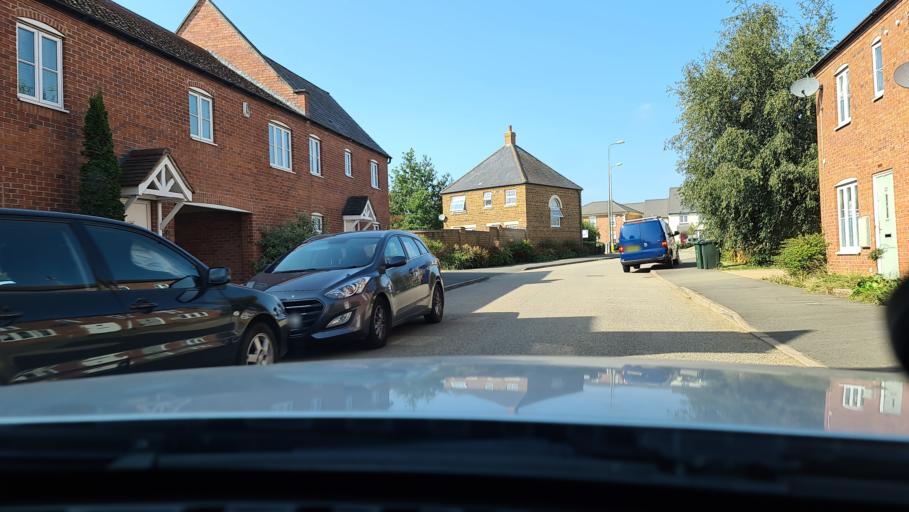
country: GB
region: England
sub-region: Oxfordshire
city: Hanwell
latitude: 52.0801
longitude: -1.3597
